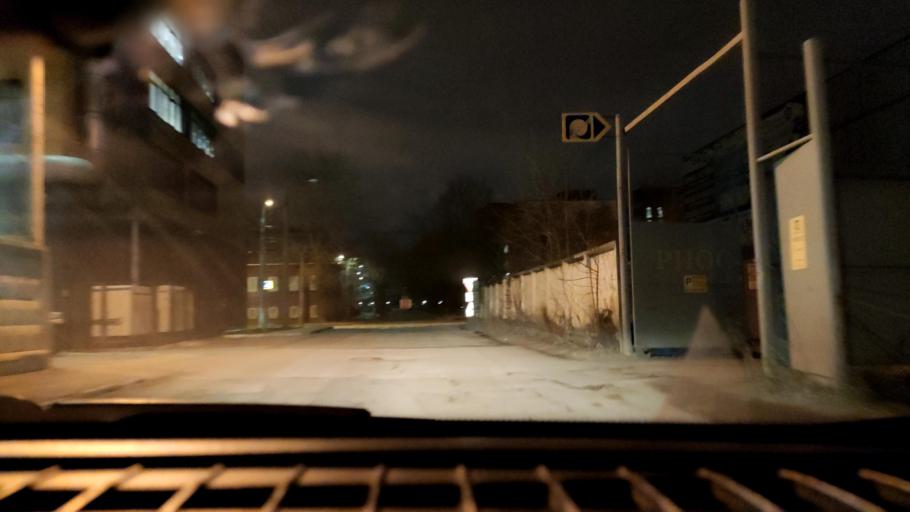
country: RU
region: Perm
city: Perm
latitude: 58.0099
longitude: 56.1867
